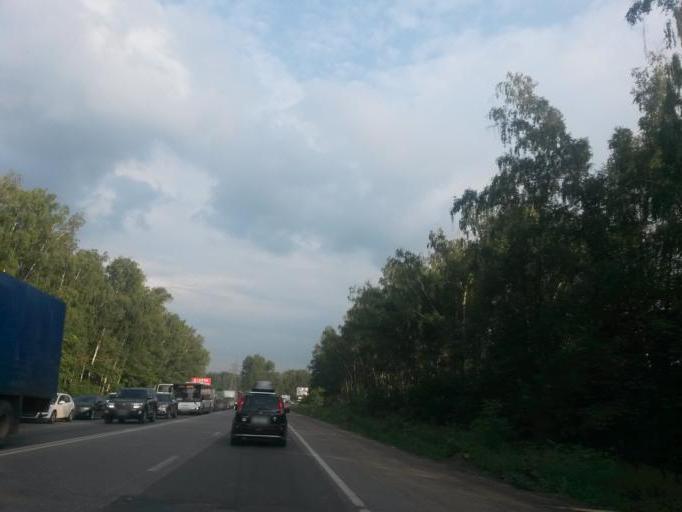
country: RU
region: Moskovskaya
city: Petrovskaya
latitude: 55.5601
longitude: 37.7725
